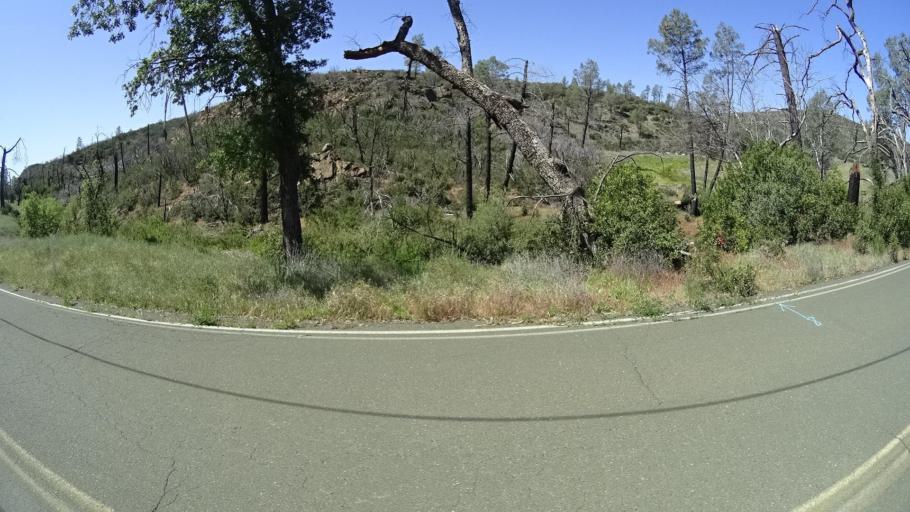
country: US
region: California
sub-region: Lake County
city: Hidden Valley Lake
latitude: 38.8562
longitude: -122.4012
